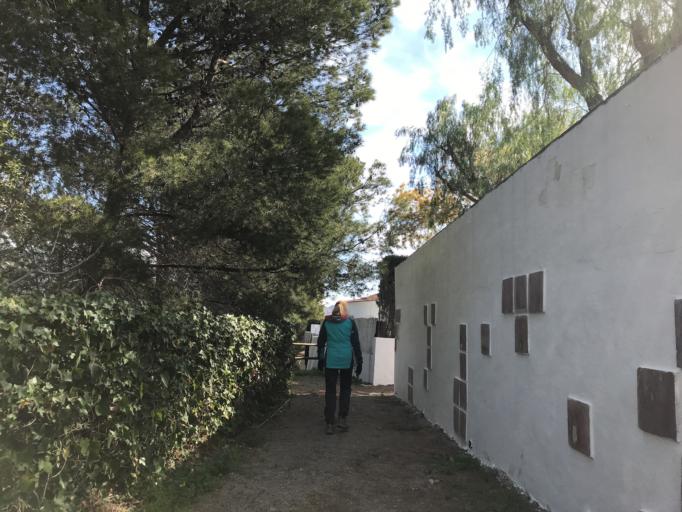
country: ES
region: Andalusia
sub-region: Provincia de Malaga
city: Valdes
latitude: 36.7623
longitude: -4.2164
